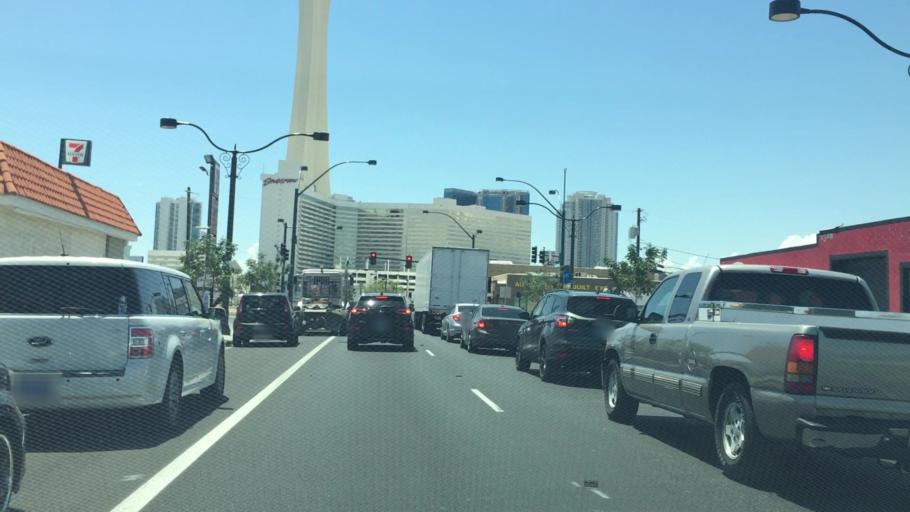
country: US
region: Nevada
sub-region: Clark County
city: Las Vegas
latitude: 36.1530
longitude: -115.1554
